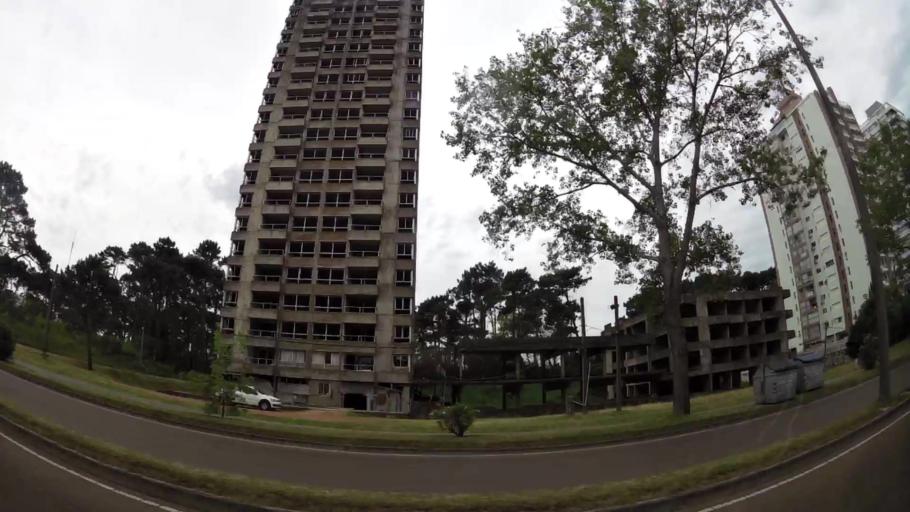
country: UY
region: Maldonado
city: Maldonado
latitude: -34.9279
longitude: -54.9466
